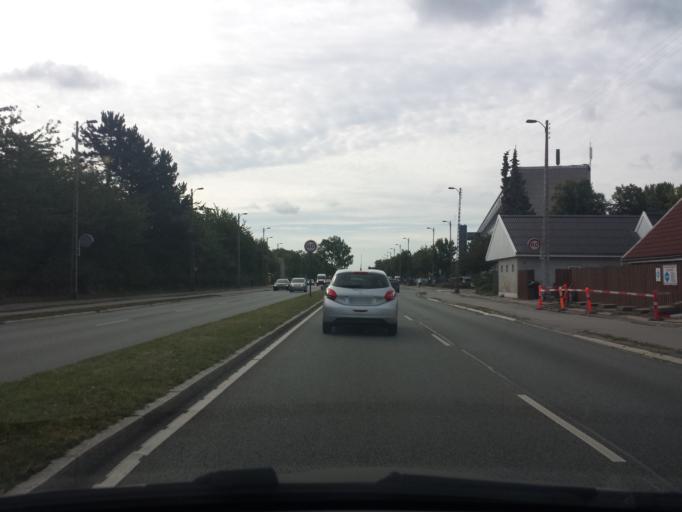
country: DK
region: Capital Region
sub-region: Rodovre Kommune
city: Rodovre
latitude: 55.6846
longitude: 12.4515
